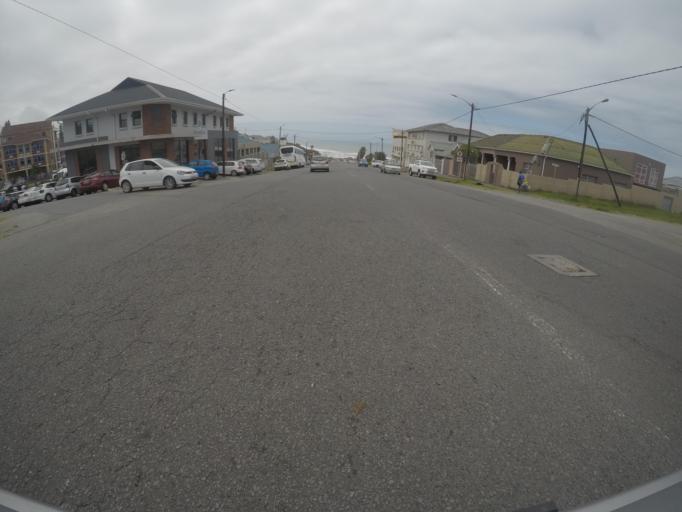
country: ZA
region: Eastern Cape
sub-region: Buffalo City Metropolitan Municipality
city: East London
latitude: -33.0124
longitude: 27.9179
